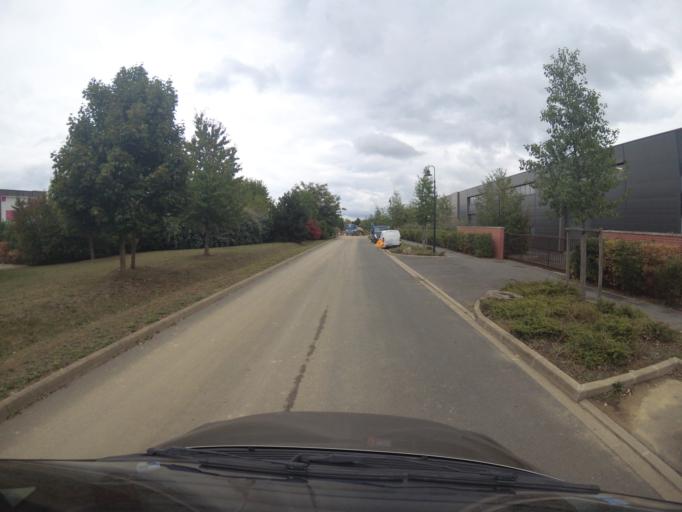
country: FR
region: Ile-de-France
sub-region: Departement de Seine-et-Marne
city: Chessy
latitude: 48.8791
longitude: 2.7762
